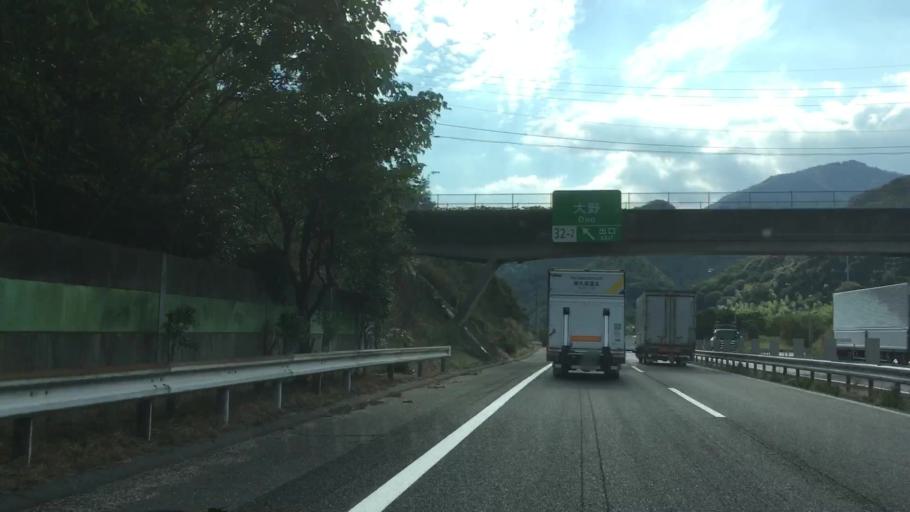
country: JP
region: Hiroshima
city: Ono-hara
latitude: 34.3013
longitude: 132.2751
